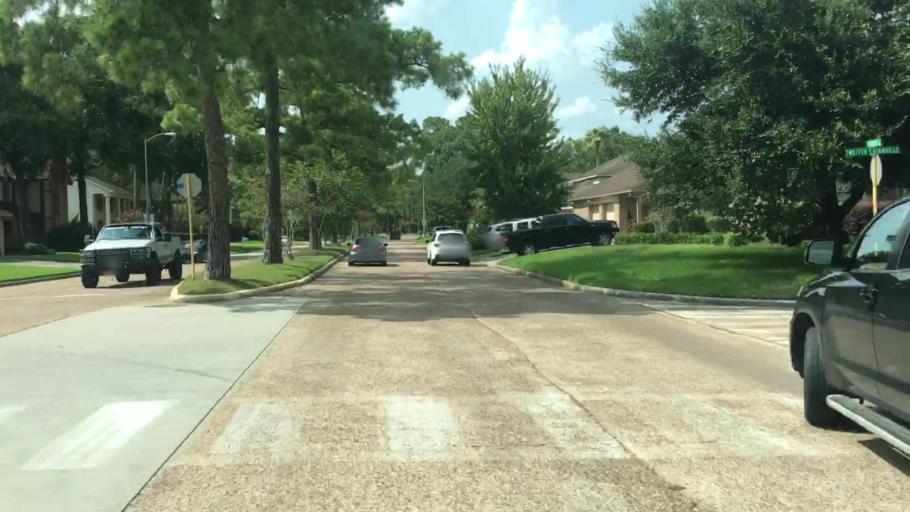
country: US
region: Texas
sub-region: Harris County
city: Atascocita
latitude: 30.0046
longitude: -95.1554
